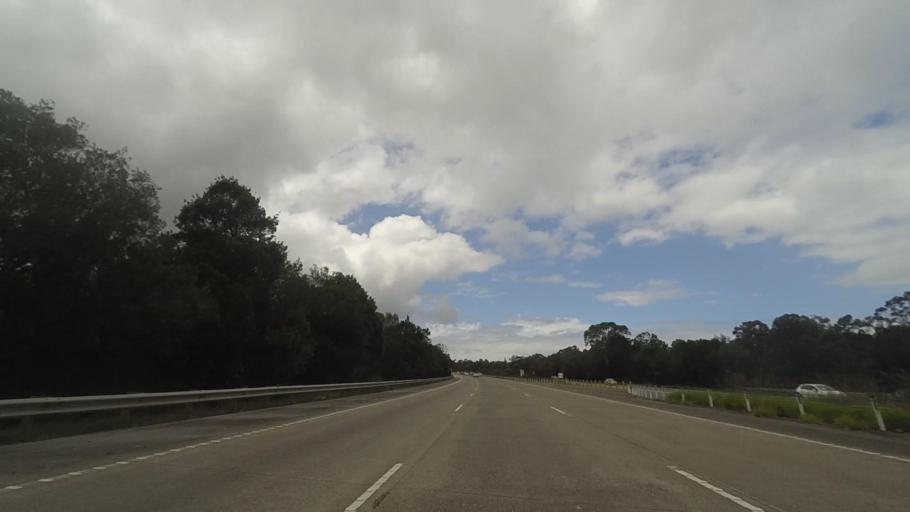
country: AU
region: New South Wales
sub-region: Gosford Shire
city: Point Clare
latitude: -33.4209
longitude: 151.2903
